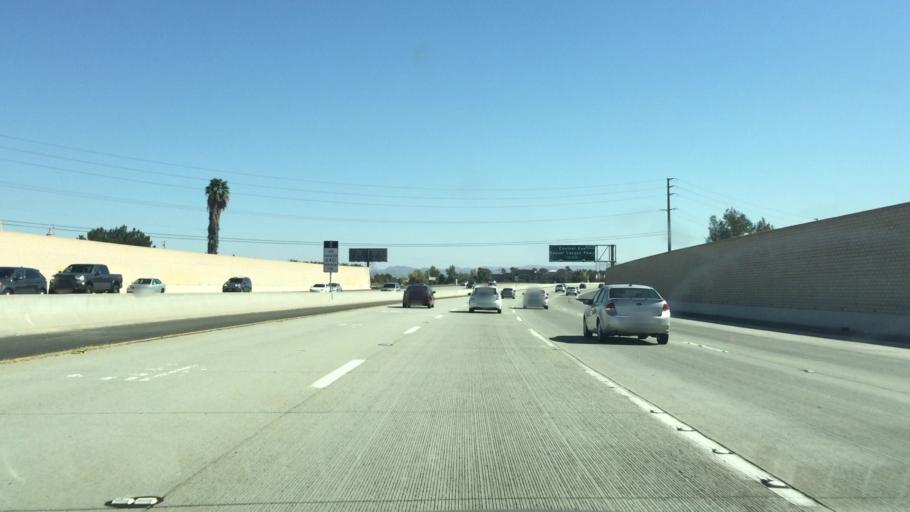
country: US
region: California
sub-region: San Bernardino County
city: Los Serranos
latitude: 33.9767
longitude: -117.6992
